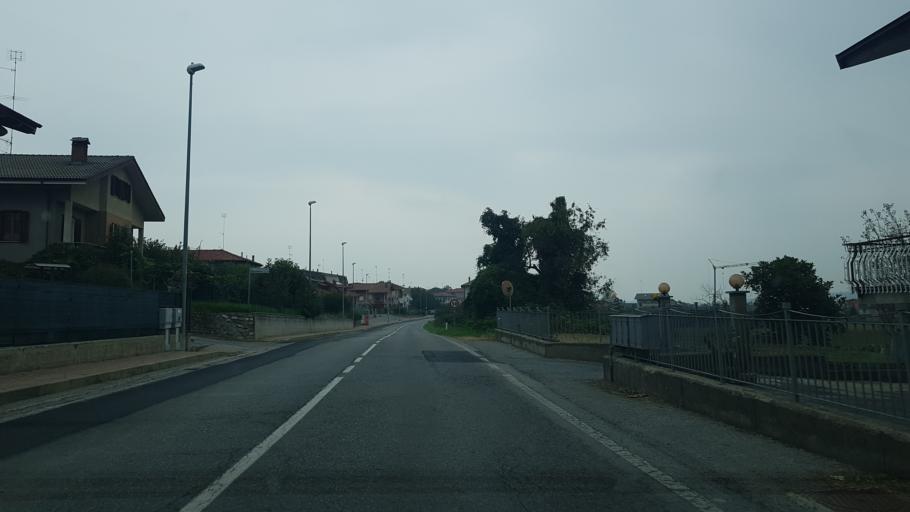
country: IT
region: Piedmont
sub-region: Provincia di Cuneo
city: Villanova Mondovi
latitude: 44.3393
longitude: 7.7623
